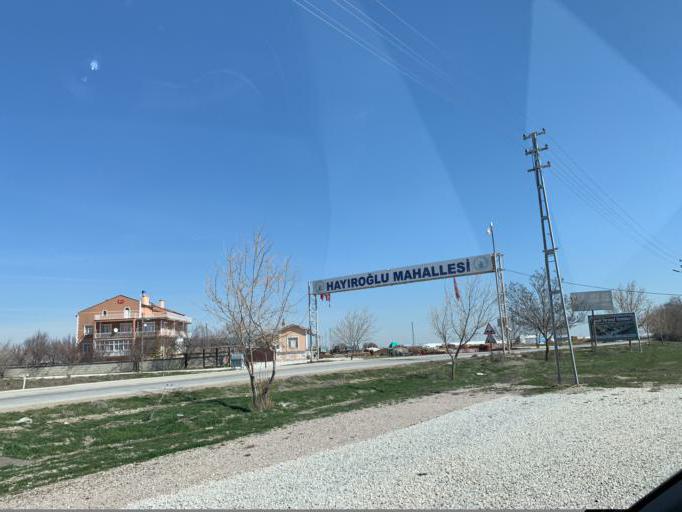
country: TR
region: Konya
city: Yarma
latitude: 37.7522
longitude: 32.8654
